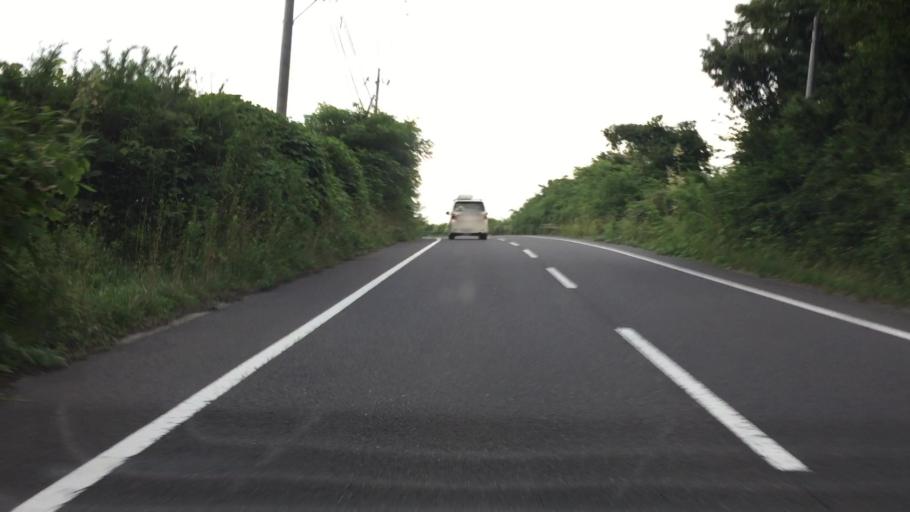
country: JP
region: Tochigi
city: Kuroiso
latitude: 37.0792
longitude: 140.0514
